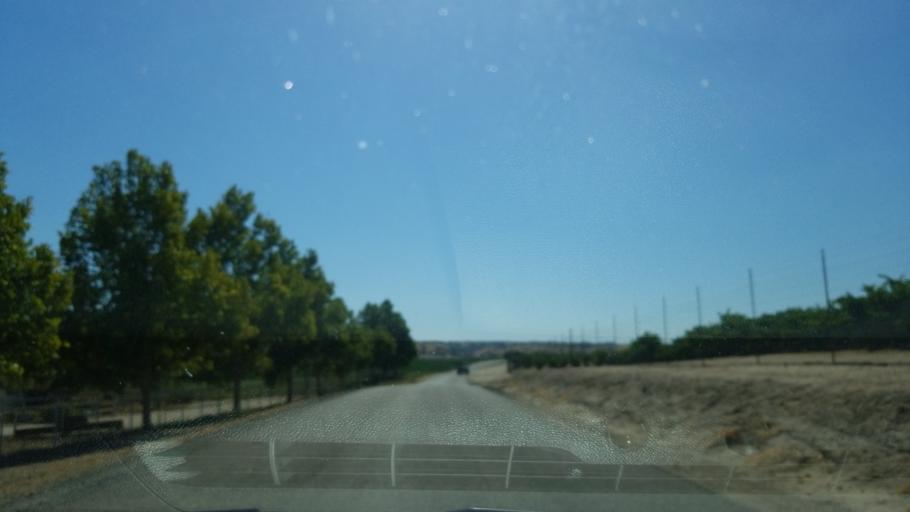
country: US
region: California
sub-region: San Luis Obispo County
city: San Miguel
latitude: 35.7365
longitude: -120.6749
